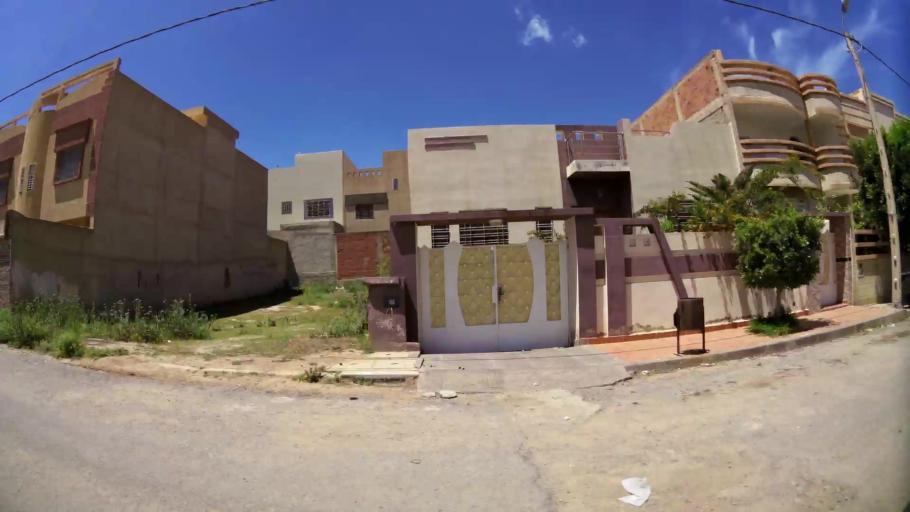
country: MA
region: Oriental
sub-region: Oujda-Angad
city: Oujda
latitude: 34.6587
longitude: -1.9444
